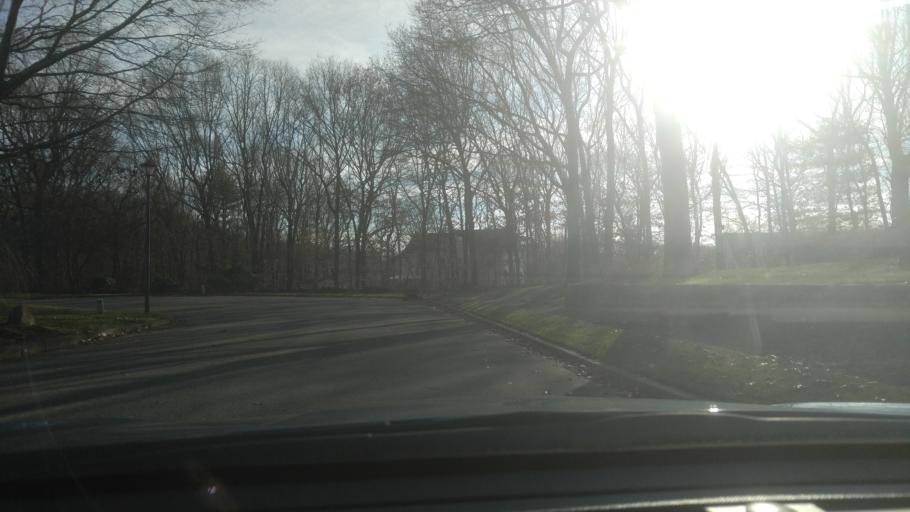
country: US
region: Rhode Island
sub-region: Kent County
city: East Greenwich
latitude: 41.6795
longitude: -71.4721
